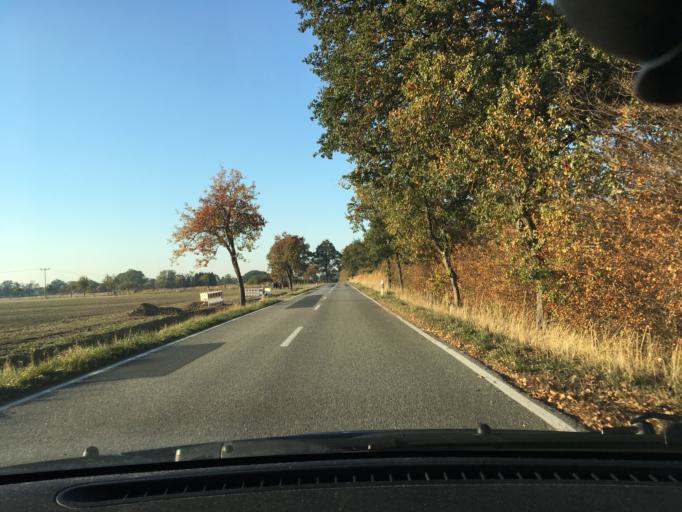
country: DE
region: Lower Saxony
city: Bleckede
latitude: 53.2959
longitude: 10.8010
